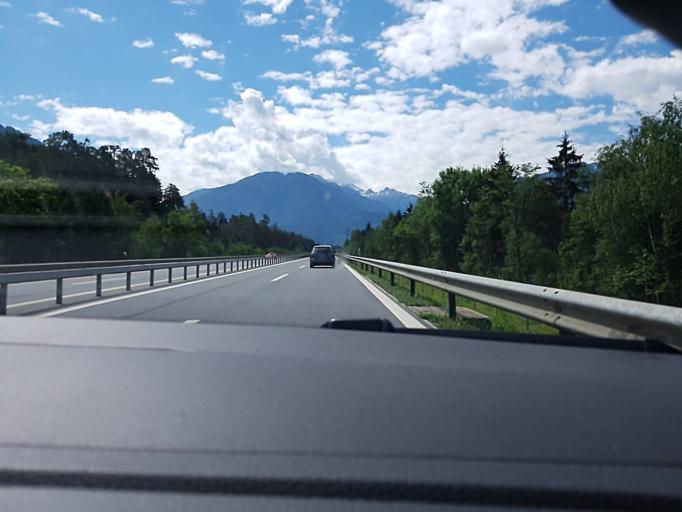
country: CH
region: Grisons
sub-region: Hinterrhein District
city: Cazis
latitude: 46.7521
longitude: 9.4281
